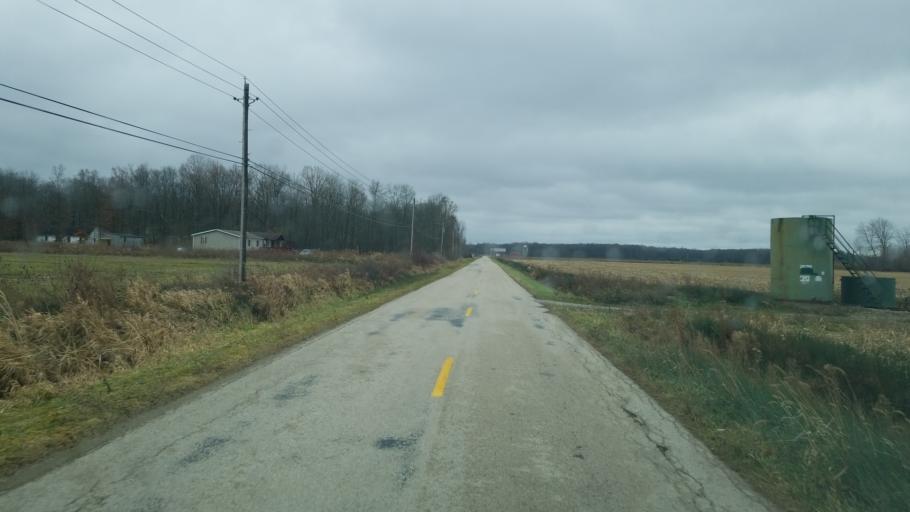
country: US
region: Ohio
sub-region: Ashtabula County
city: Roaming Shores
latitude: 41.6145
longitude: -80.8259
